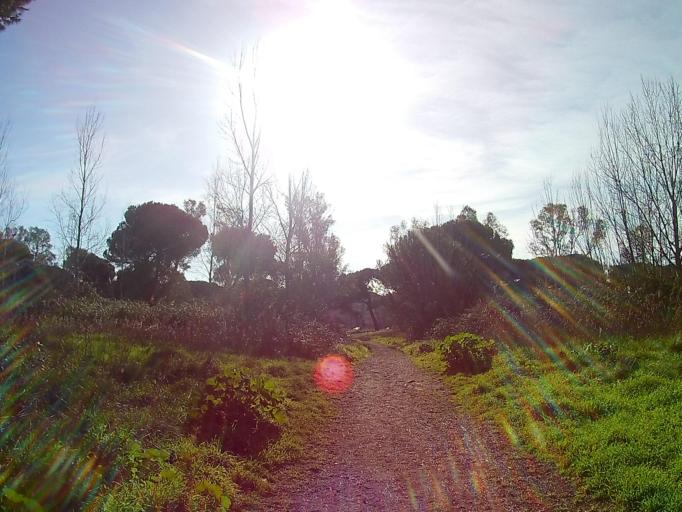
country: IT
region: Latium
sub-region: Citta metropolitana di Roma Capitale
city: Lido di Ostia
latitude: 41.7434
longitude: 12.2709
